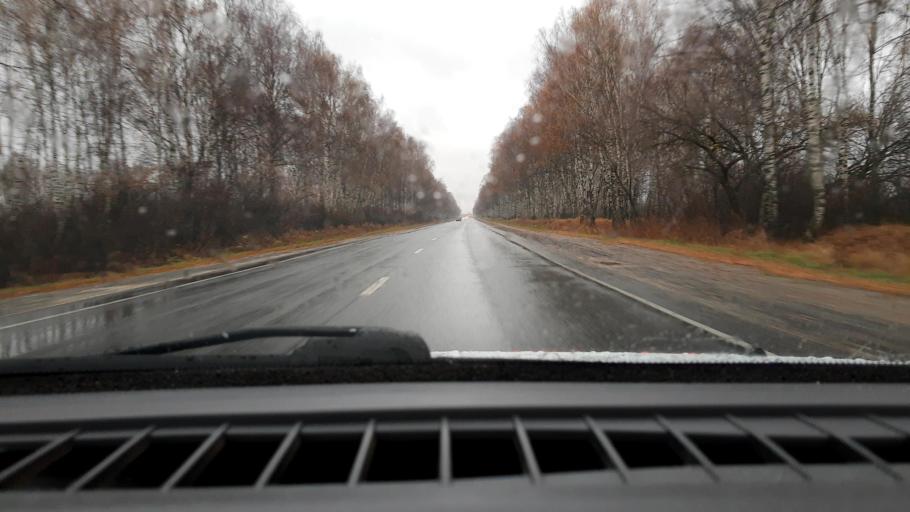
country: RU
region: Nizjnij Novgorod
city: Sitniki
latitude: 56.5110
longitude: 44.0237
